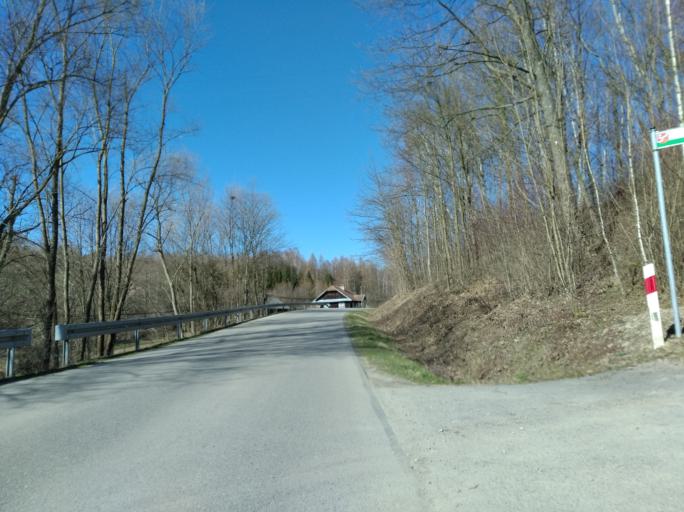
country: PL
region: Subcarpathian Voivodeship
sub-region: Powiat strzyzowski
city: Wisniowa
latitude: 49.8906
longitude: 21.6654
